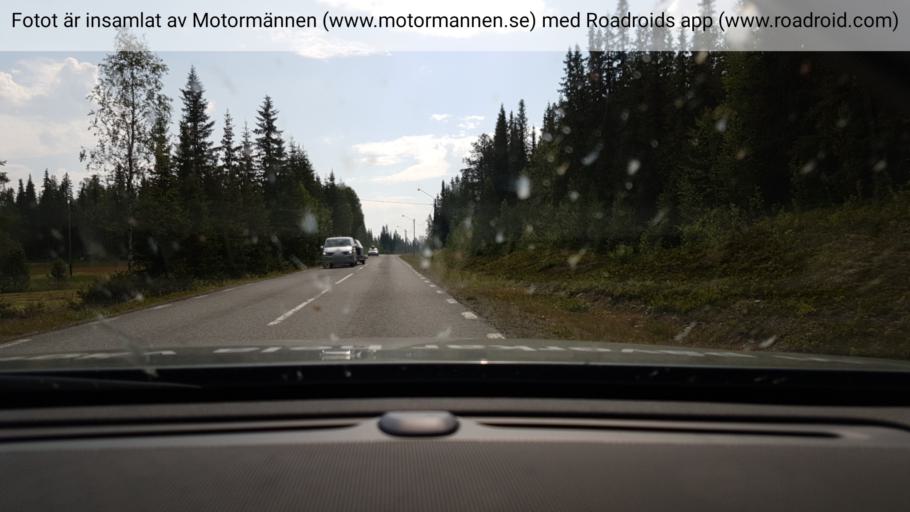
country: SE
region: Vaesterbotten
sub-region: Vilhelmina Kommun
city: Sjoberg
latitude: 65.4523
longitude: 16.0979
